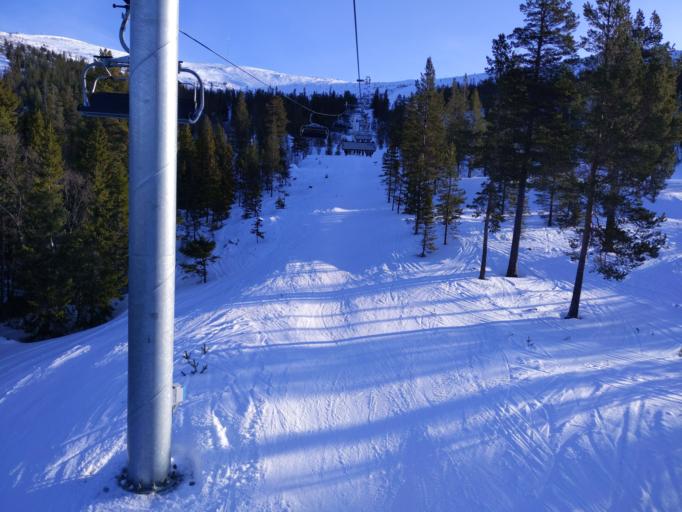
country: SE
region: Jaemtland
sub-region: Harjedalens Kommun
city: Sveg
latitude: 62.4132
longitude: 13.9689
